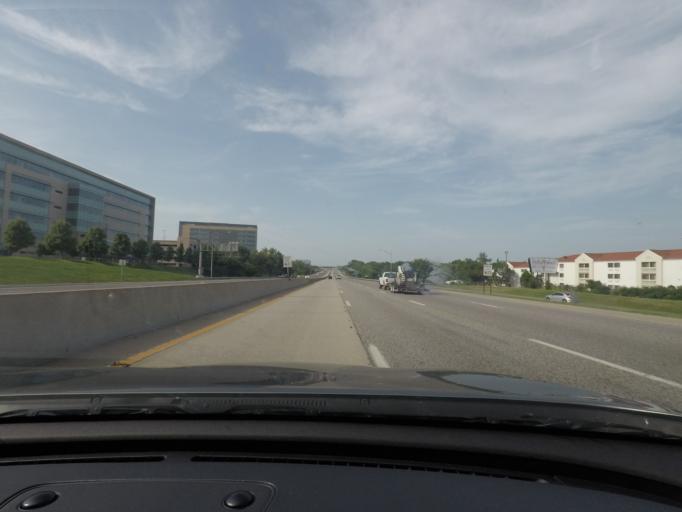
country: US
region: Missouri
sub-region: Saint Louis County
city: Maryland Heights
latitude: 38.7130
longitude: -90.4479
